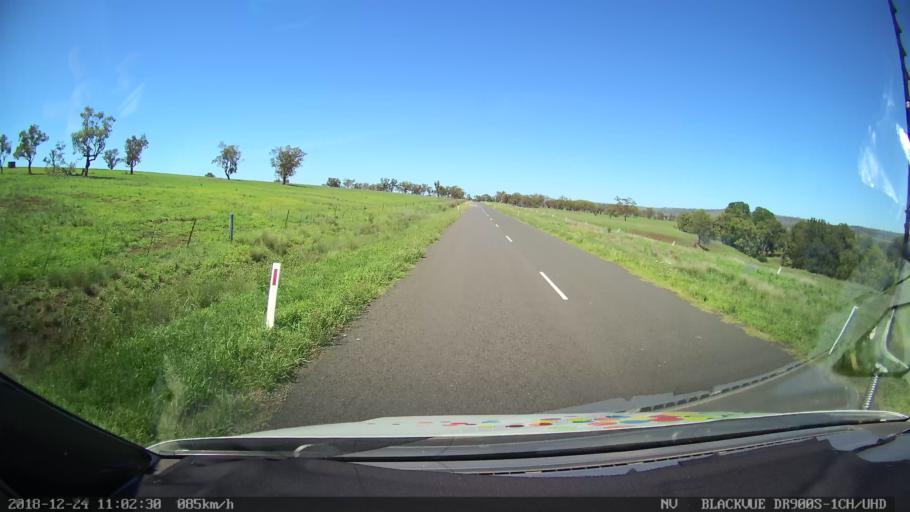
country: AU
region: New South Wales
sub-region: Upper Hunter Shire
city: Merriwa
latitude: -32.0857
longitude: 150.3747
